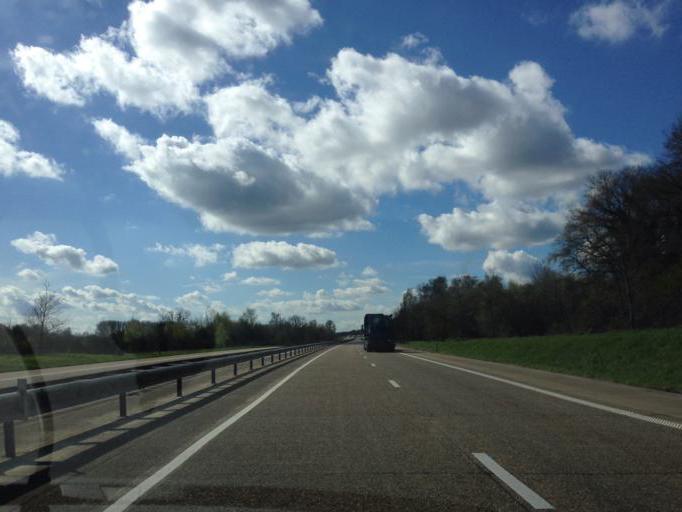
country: BE
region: Flanders
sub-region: Provincie Limburg
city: Helchteren
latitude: 51.1027
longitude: 5.3771
